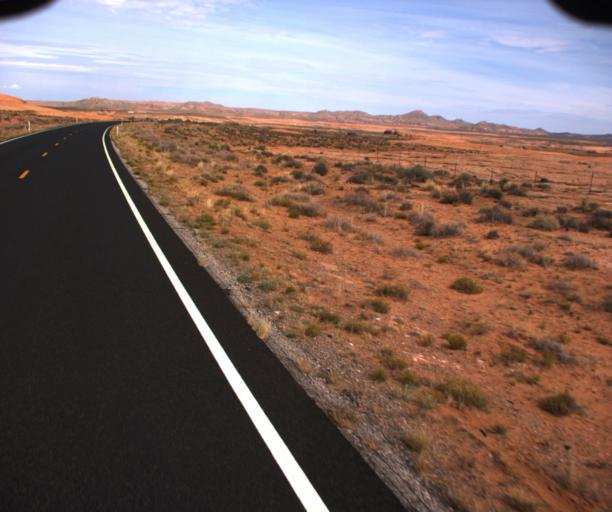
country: US
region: Arizona
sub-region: Apache County
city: Many Farms
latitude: 36.9117
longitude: -109.6233
